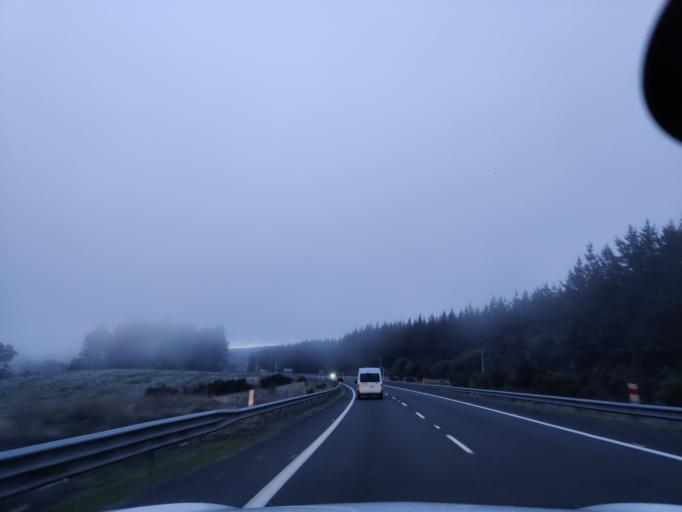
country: NZ
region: Waikato
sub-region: South Waikato District
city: Tokoroa
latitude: -38.3928
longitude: 176.0140
